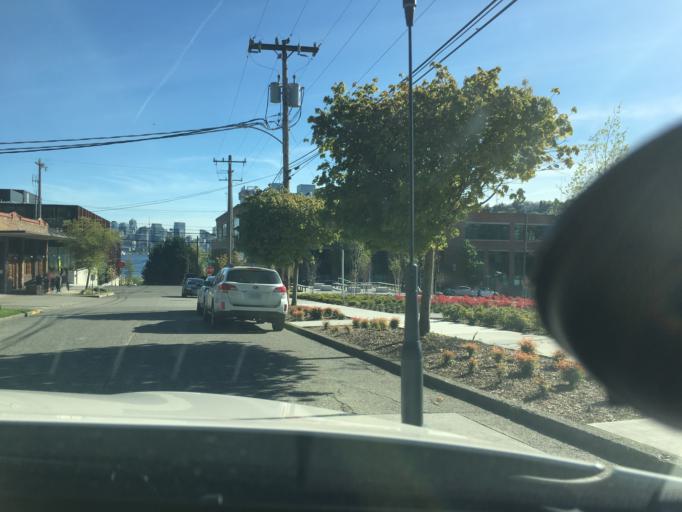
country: US
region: Washington
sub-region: King County
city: Seattle
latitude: 47.6487
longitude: -122.3387
